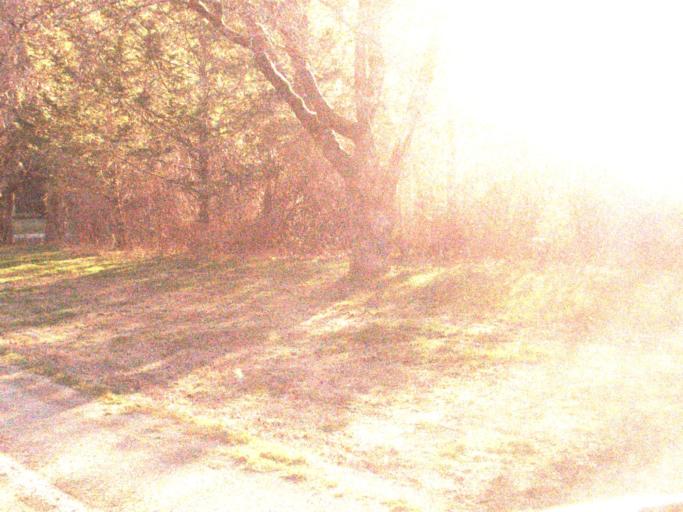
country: US
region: Washington
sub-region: Snohomish County
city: Darrington
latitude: 48.6729
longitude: -121.2577
